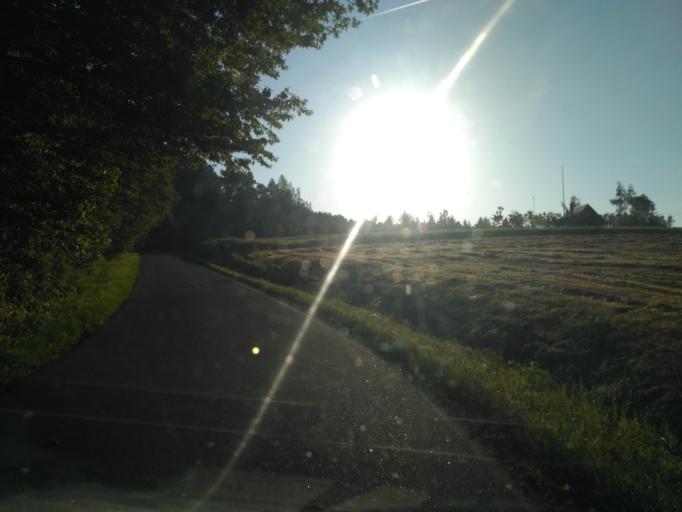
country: PL
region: Subcarpathian Voivodeship
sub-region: Powiat strzyzowski
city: Polomia
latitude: 49.9040
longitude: 21.8926
